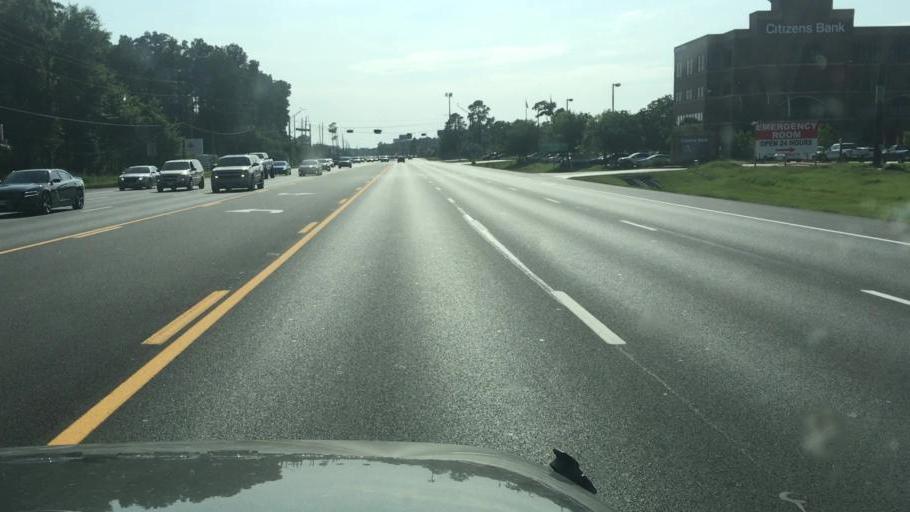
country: US
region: Texas
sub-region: Harris County
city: Humble
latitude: 30.0050
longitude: -95.2890
